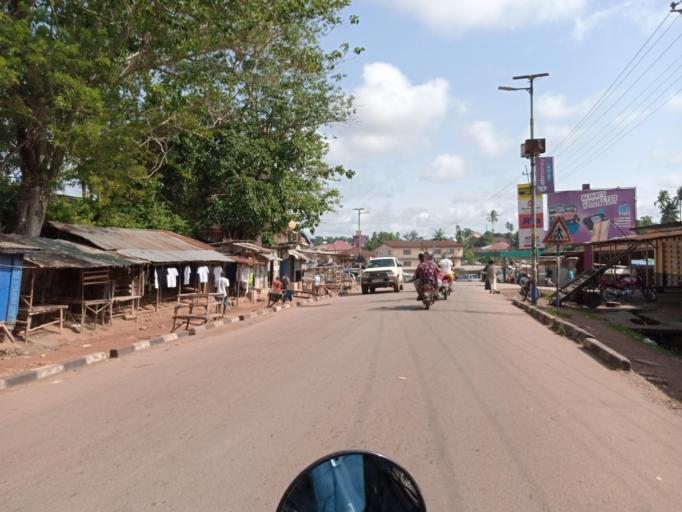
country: SL
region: Southern Province
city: Bo
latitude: 7.9635
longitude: -11.7346
